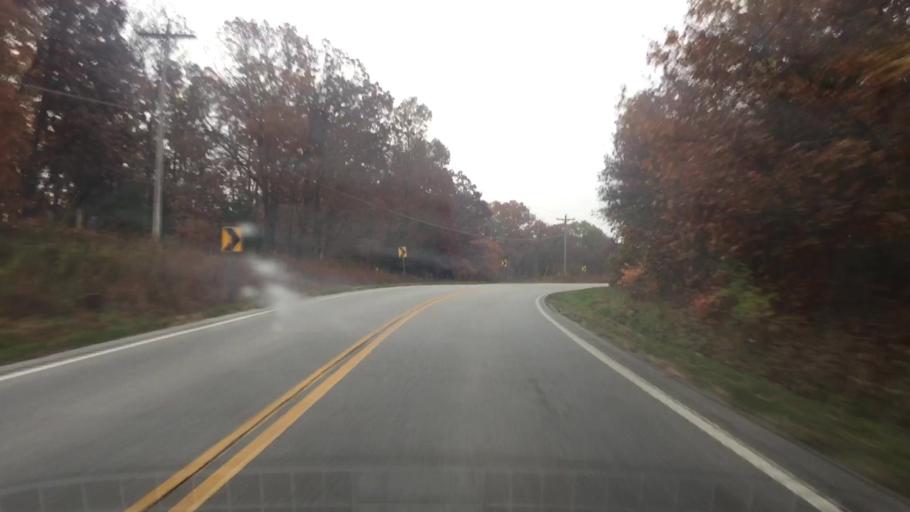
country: US
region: Missouri
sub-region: Callaway County
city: Fulton
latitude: 38.8801
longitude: -92.0868
